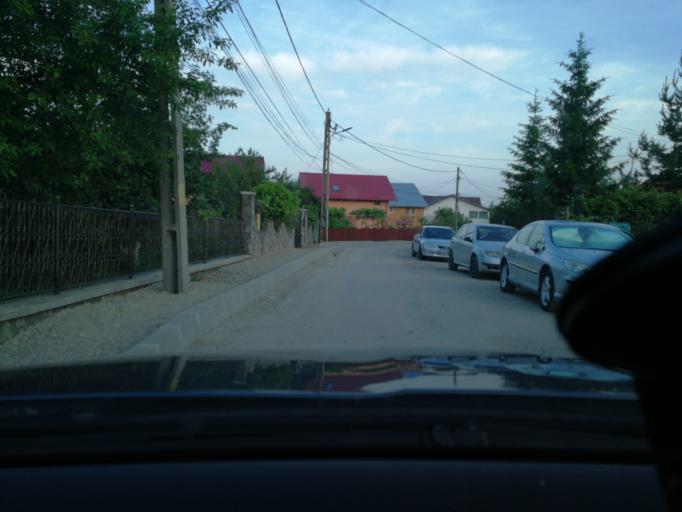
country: RO
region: Prahova
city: Cornu de Sus
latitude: 45.1600
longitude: 25.6980
